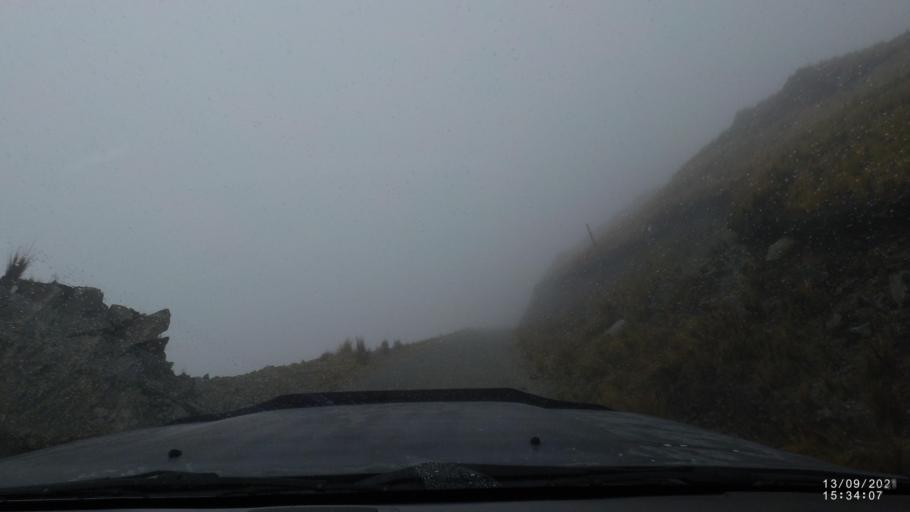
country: BO
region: Cochabamba
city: Colomi
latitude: -17.3361
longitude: -65.7409
